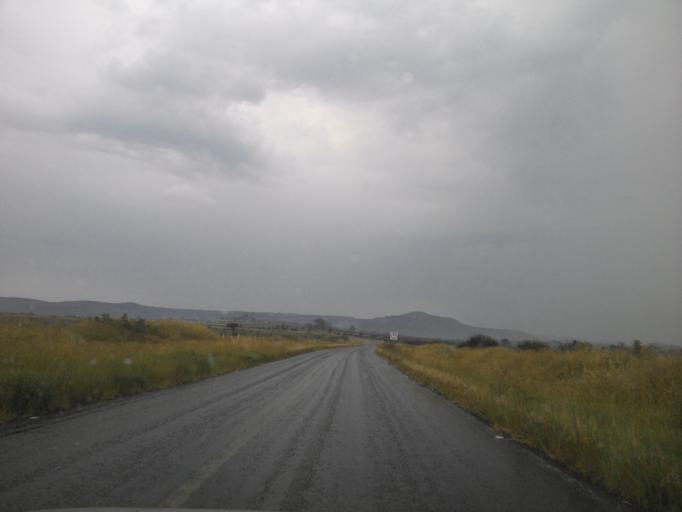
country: MX
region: Jalisco
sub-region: Arandas
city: Santiaguito (Santiaguito de Velazquez)
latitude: 20.8391
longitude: -102.1046
